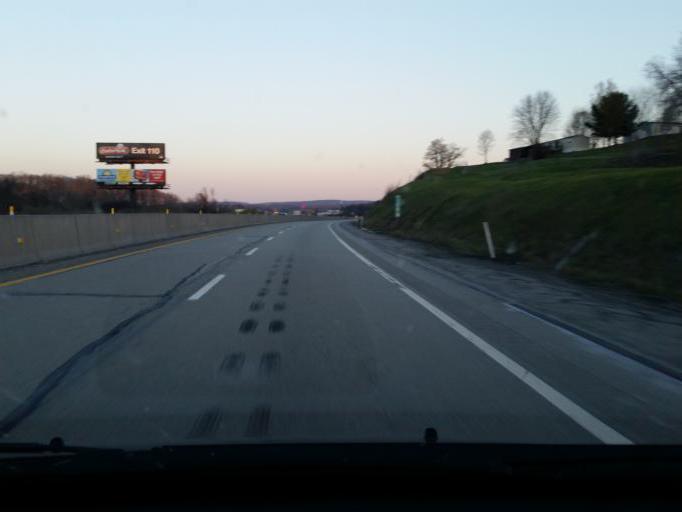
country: US
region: Pennsylvania
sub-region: Somerset County
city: Somerset
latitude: 40.0322
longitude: -79.0952
